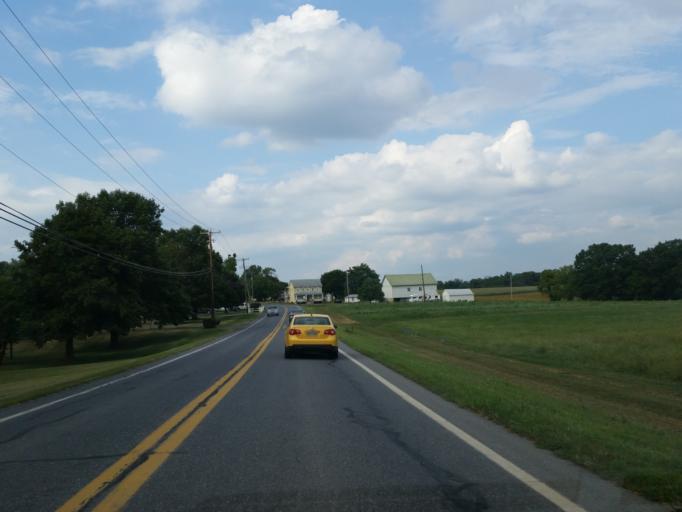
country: US
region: Pennsylvania
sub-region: Lebanon County
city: Jonestown
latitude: 40.3930
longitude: -76.5234
